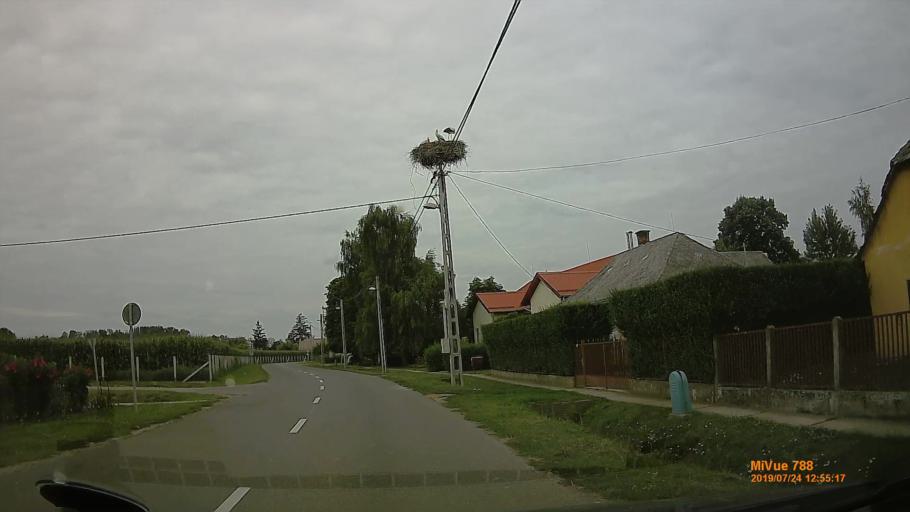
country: HU
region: Szabolcs-Szatmar-Bereg
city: Aranyosapati
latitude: 48.2232
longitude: 22.2925
